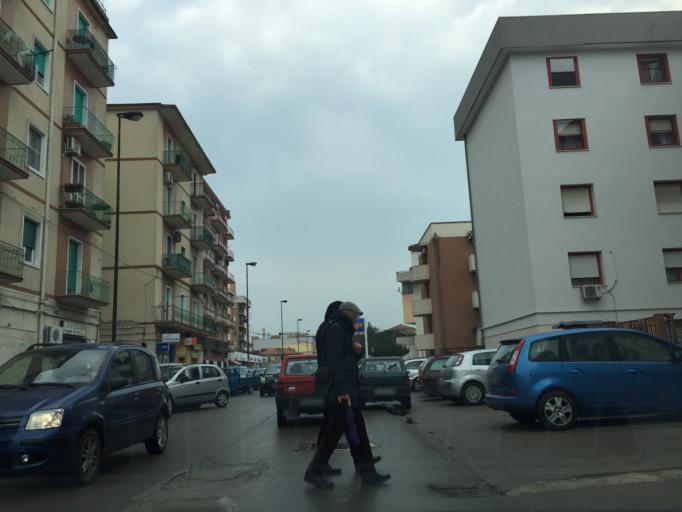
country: IT
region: Apulia
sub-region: Provincia di Foggia
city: Foggia
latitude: 41.4657
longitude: 15.5366
